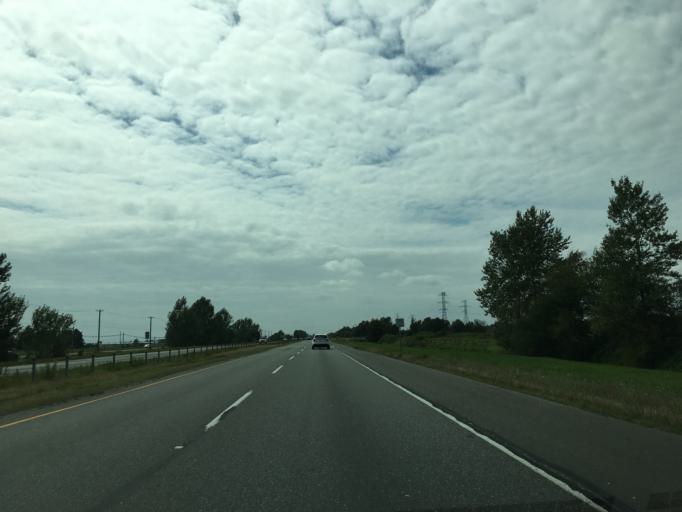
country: CA
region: British Columbia
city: Delta
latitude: 49.0905
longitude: -122.9726
